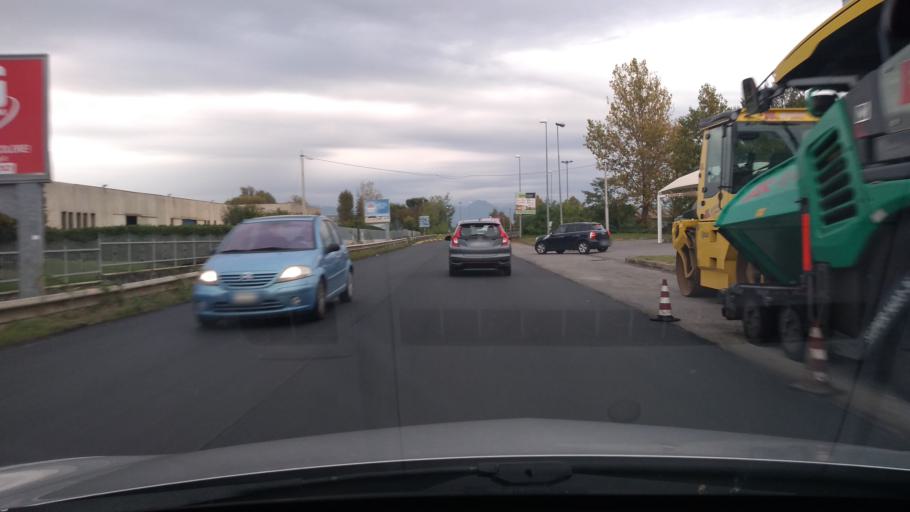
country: IT
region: Lombardy
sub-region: Provincia di Bergamo
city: Verdello
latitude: 45.6151
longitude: 9.6321
